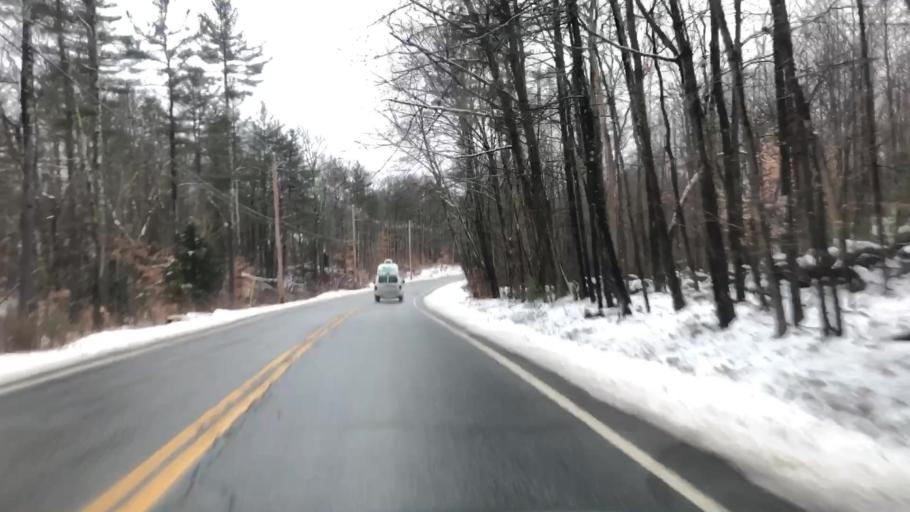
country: US
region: New Hampshire
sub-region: Hillsborough County
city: New Boston
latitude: 43.0163
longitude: -71.6886
